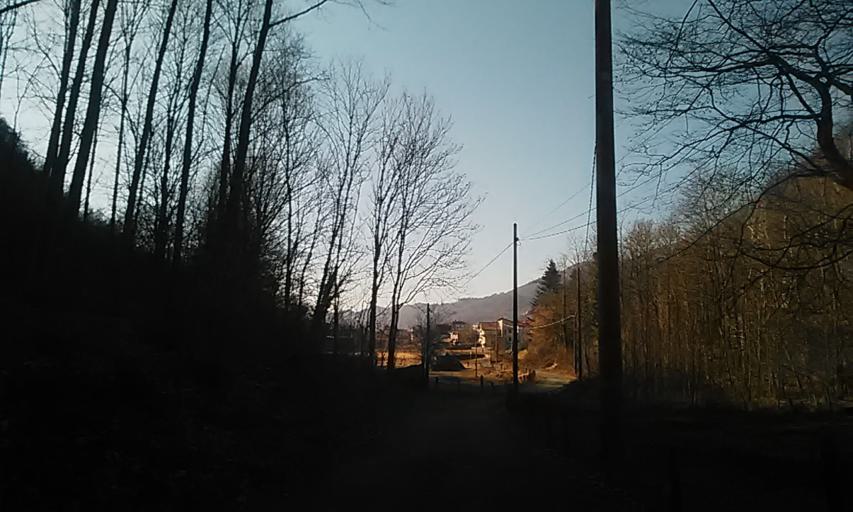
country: IT
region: Piedmont
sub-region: Provincia di Vercelli
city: Quarona
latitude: 45.7687
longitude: 8.2732
